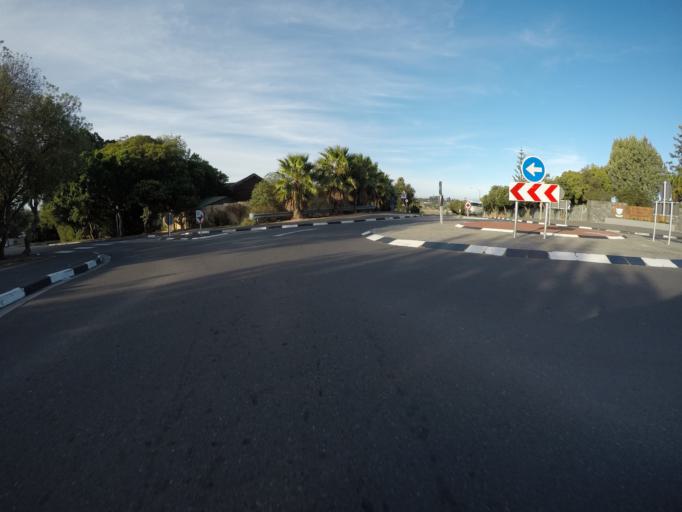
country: ZA
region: Western Cape
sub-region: City of Cape Town
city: Kraaifontein
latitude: -33.8633
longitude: 18.6605
